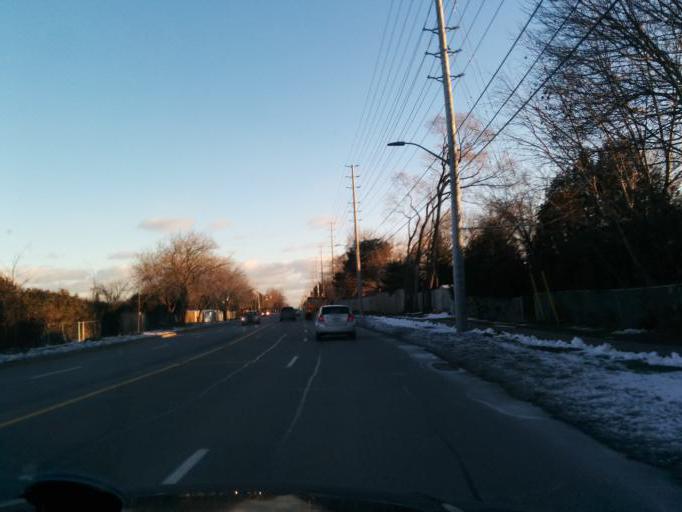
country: CA
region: Ontario
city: Mississauga
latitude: 43.6122
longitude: -79.6102
